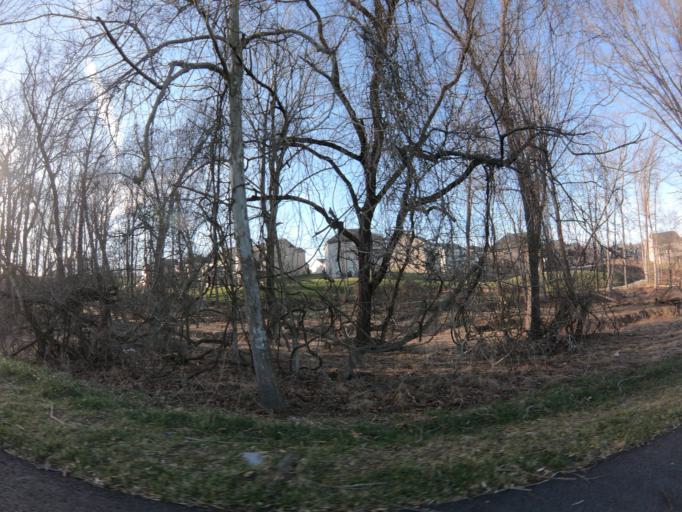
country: US
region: Maryland
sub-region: Howard County
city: Ellicott City
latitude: 39.3036
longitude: -76.8186
